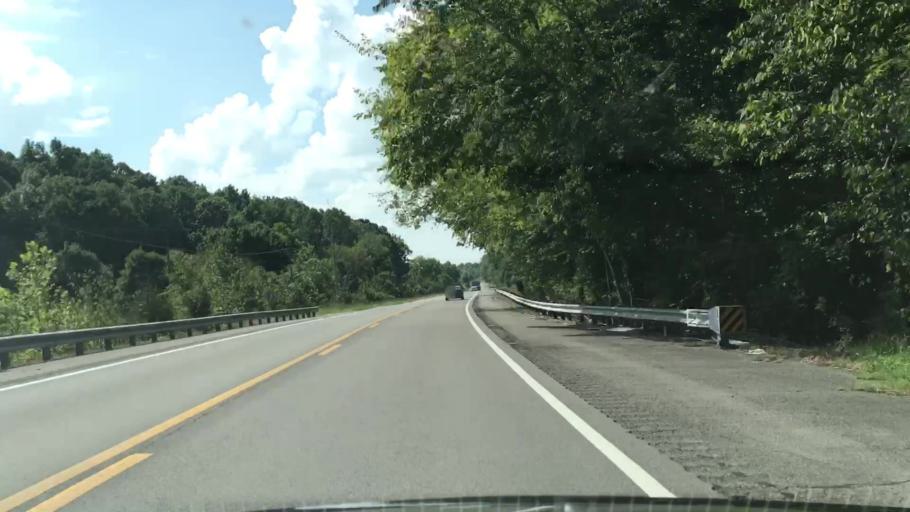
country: US
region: Tennessee
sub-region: Sumner County
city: Westmoreland
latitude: 36.6273
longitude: -86.2381
